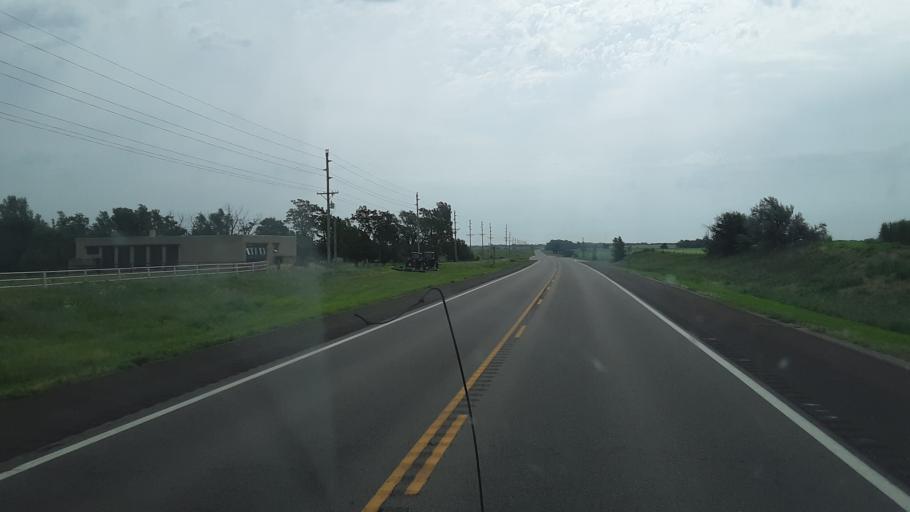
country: US
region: Kansas
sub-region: Stafford County
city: Stafford
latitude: 37.9548
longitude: -98.4948
